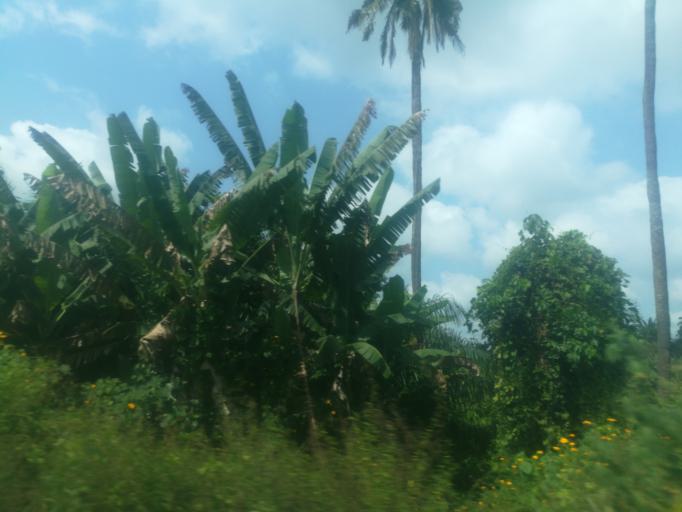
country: NG
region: Oyo
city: Moniya
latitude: 7.5785
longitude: 3.9109
